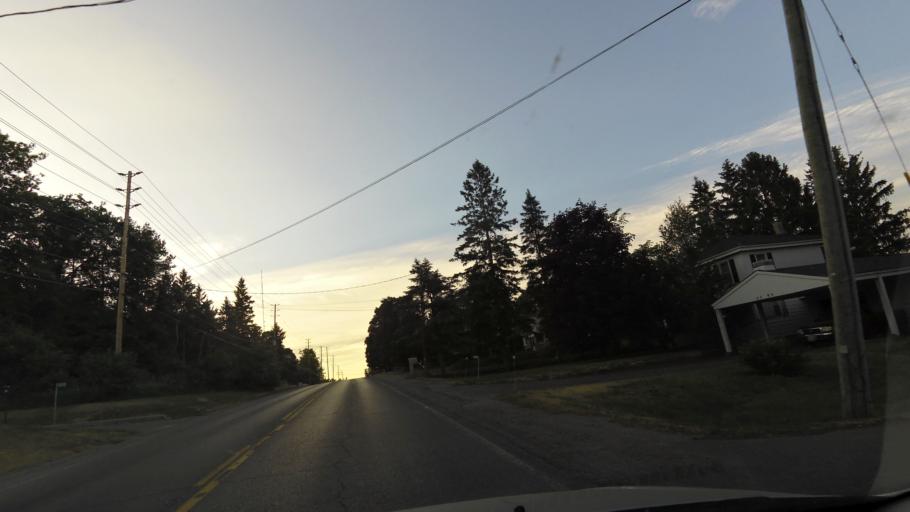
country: CA
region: Ontario
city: Peterborough
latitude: 44.3183
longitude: -78.2912
